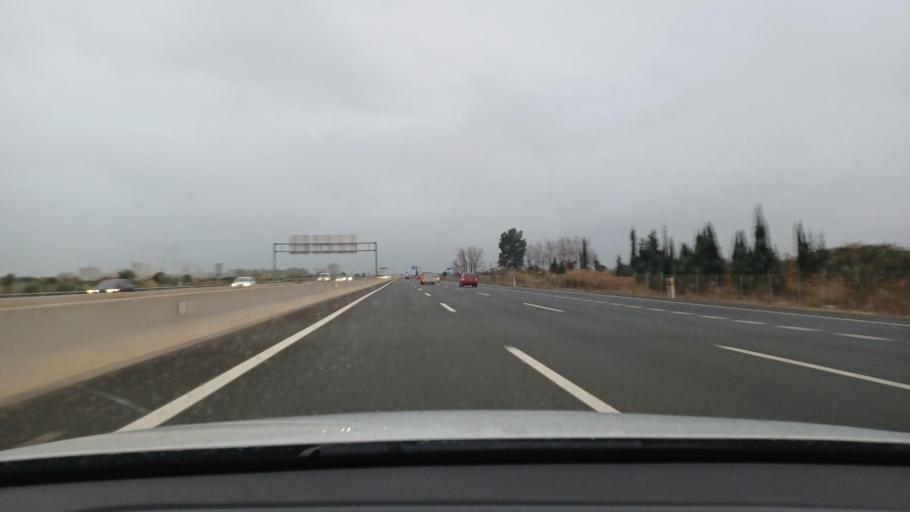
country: ES
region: Valencia
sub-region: Provincia de Valencia
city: Puig
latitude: 39.5844
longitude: -0.2941
